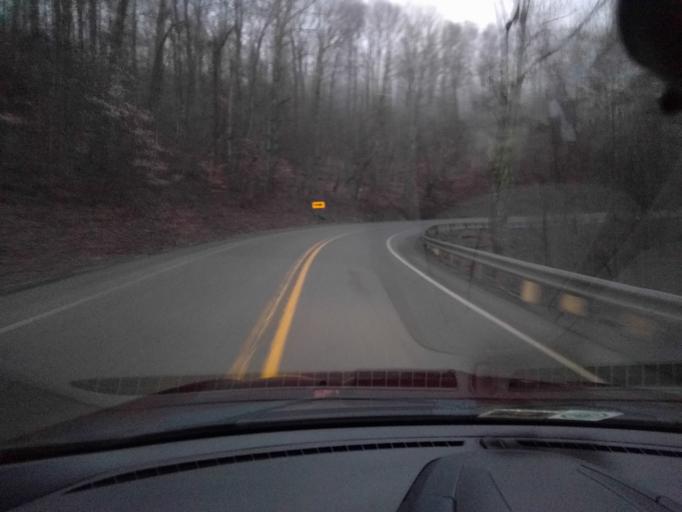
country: US
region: West Virginia
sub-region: Greenbrier County
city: Rainelle
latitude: 37.9816
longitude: -80.8376
